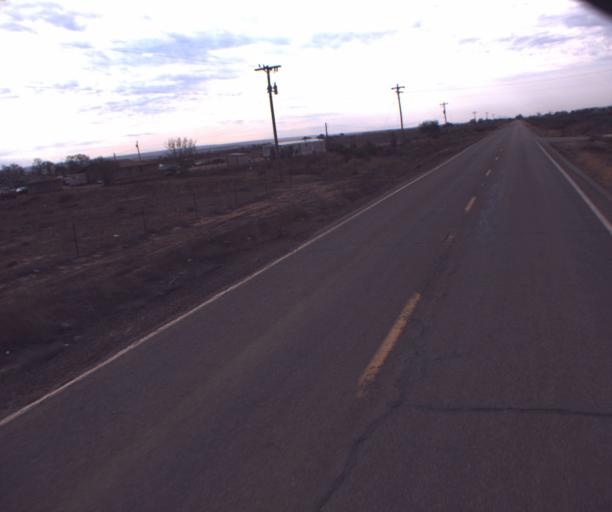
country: US
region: Arizona
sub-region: Apache County
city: Many Farms
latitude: 36.4349
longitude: -109.6070
